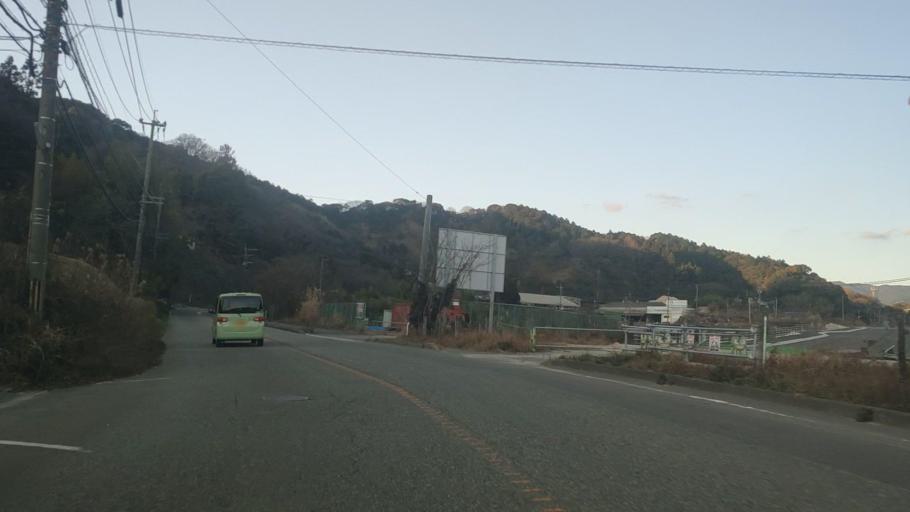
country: JP
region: Fukuoka
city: Dazaifu
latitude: 33.5419
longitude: 130.5397
